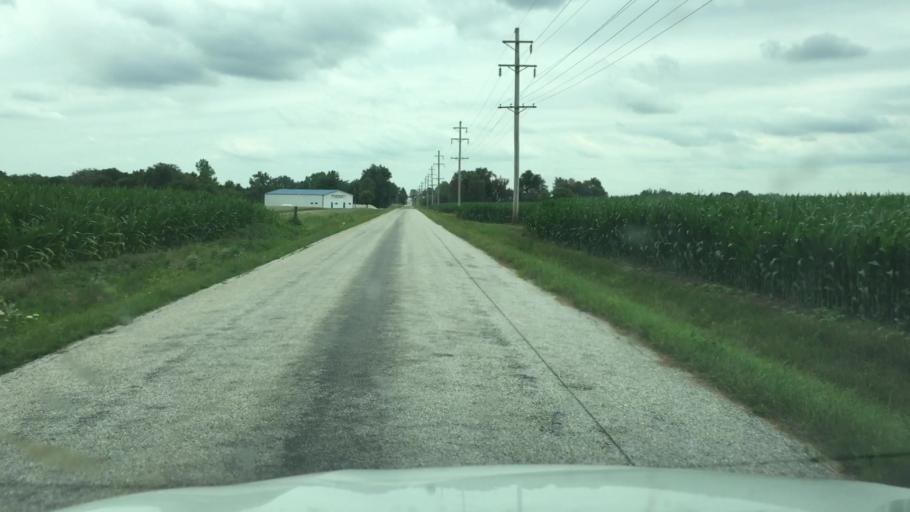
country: US
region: Illinois
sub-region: Hancock County
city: Carthage
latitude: 40.3349
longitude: -91.0825
